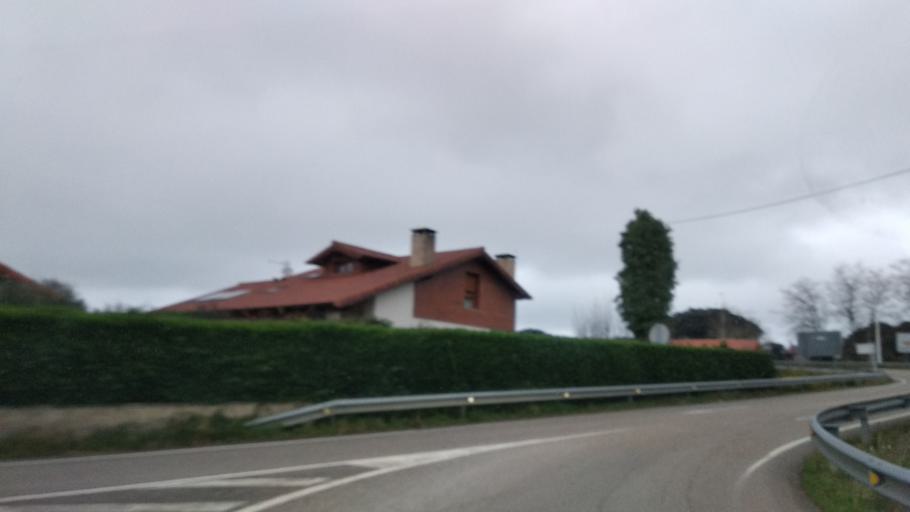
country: ES
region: Cantabria
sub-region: Provincia de Cantabria
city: Santander
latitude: 43.4493
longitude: -3.7300
